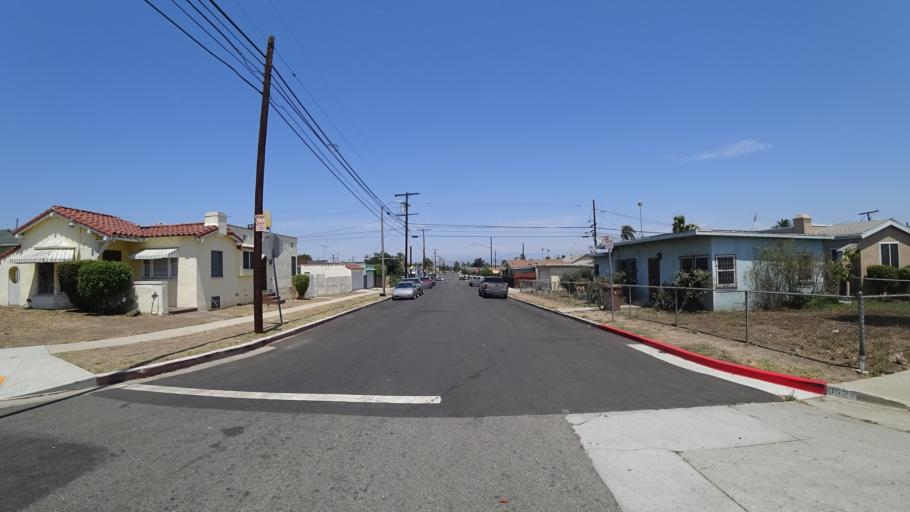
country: US
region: California
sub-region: Los Angeles County
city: Westmont
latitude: 33.9487
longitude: -118.3025
